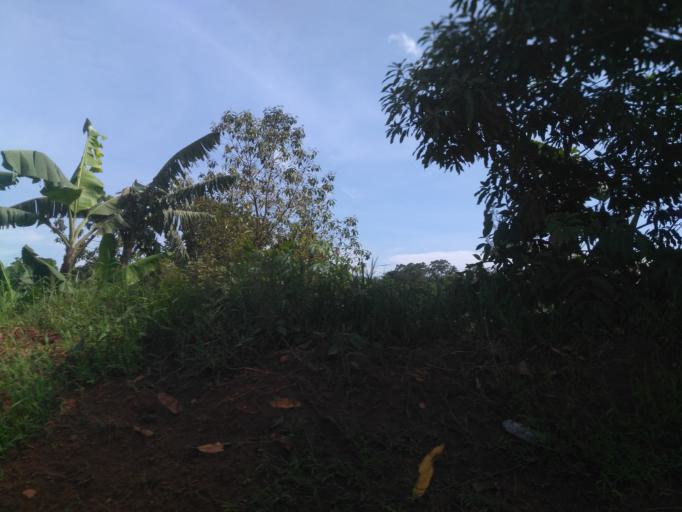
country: UG
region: Central Region
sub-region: Wakiso District
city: Kireka
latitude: 0.4444
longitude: 32.5839
